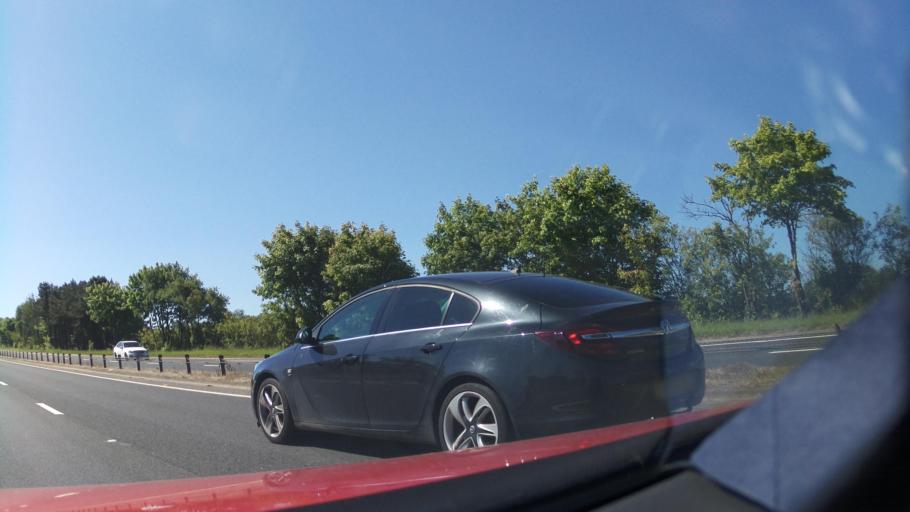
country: GB
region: Scotland
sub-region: Fife
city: Thornton
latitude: 56.1547
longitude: -3.1372
